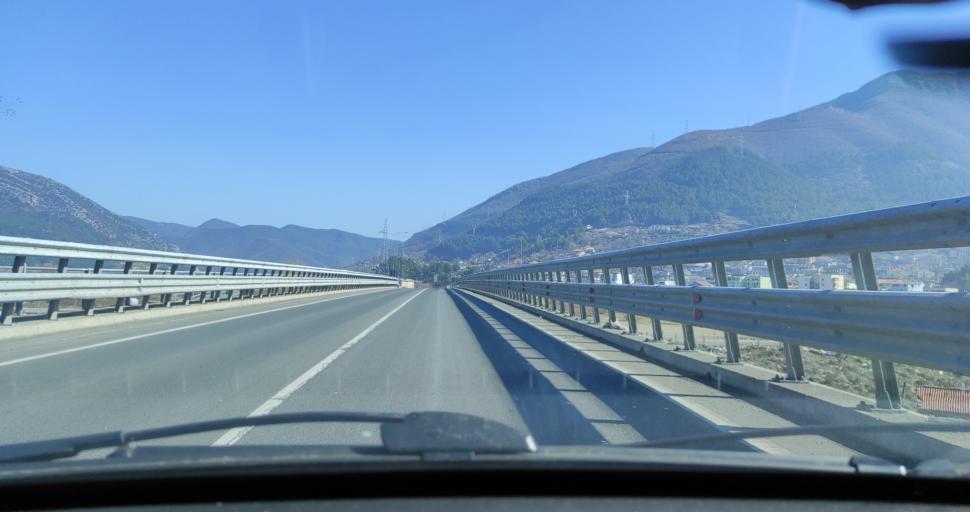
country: AL
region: Lezhe
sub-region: Rrethi i Kurbinit
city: Milot
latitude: 41.6819
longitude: 19.7093
